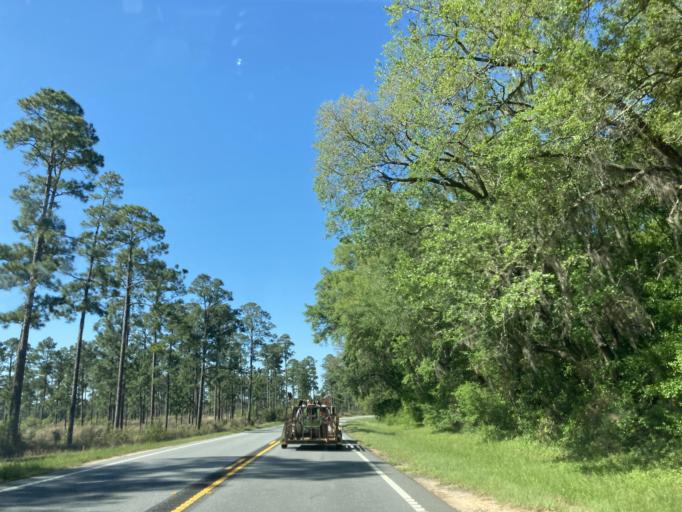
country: US
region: Georgia
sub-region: Baker County
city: Newton
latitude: 31.4280
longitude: -84.2778
